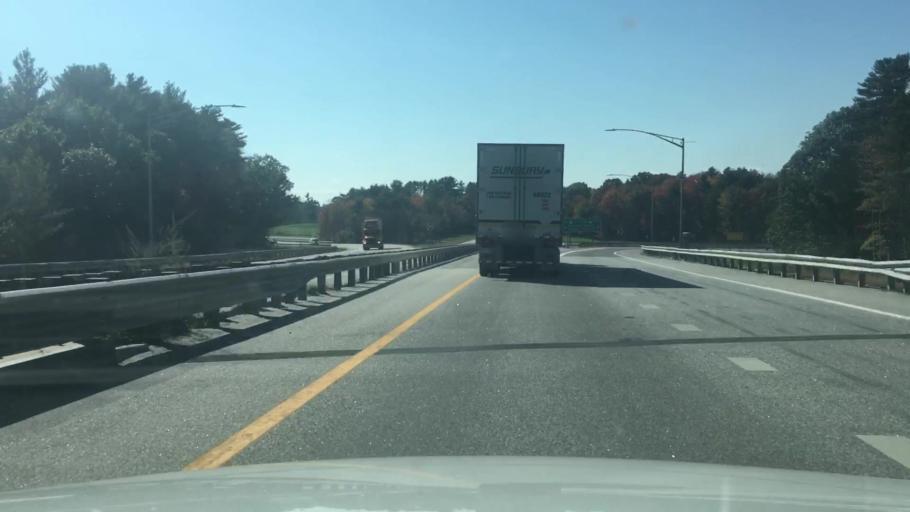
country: US
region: Maine
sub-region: Cumberland County
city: Falmouth
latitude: 43.7229
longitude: -70.3012
